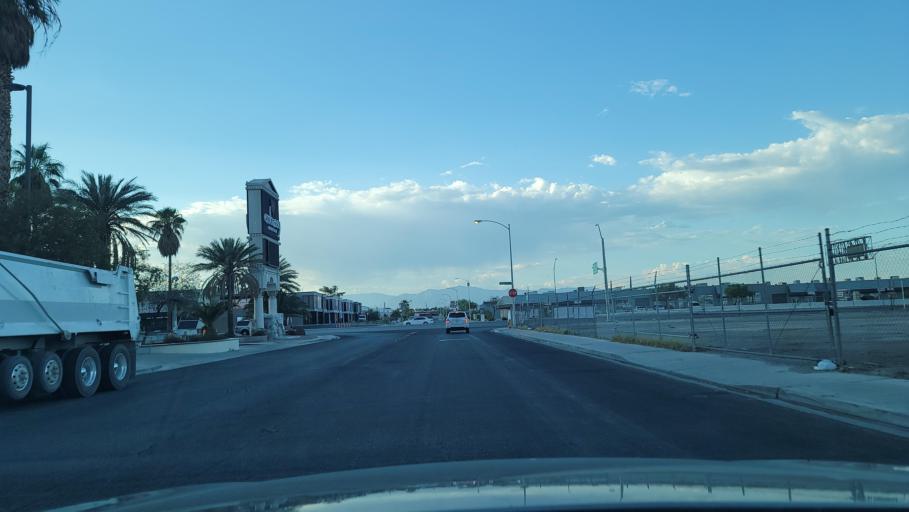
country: US
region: Nevada
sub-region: Clark County
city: Paradise
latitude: 36.1291
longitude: -115.1878
